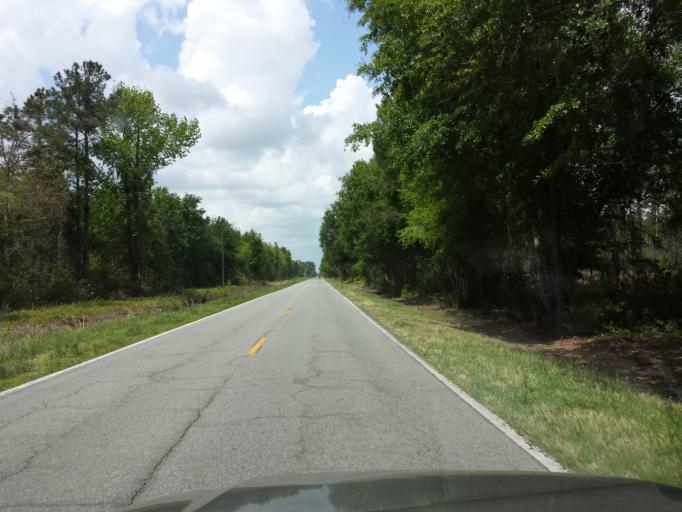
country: US
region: Georgia
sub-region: Echols County
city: Statenville
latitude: 30.6335
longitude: -83.1280
